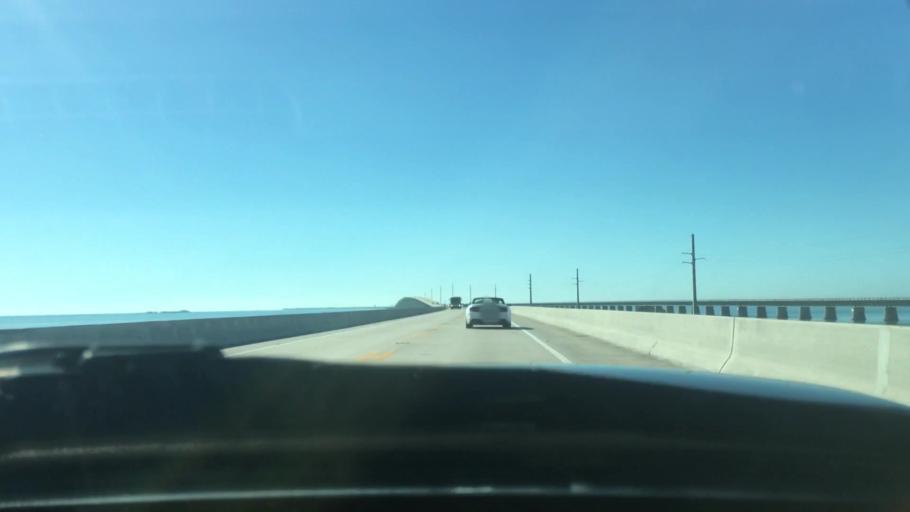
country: US
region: Florida
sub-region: Monroe County
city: Marathon
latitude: 24.7023
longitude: -81.1560
